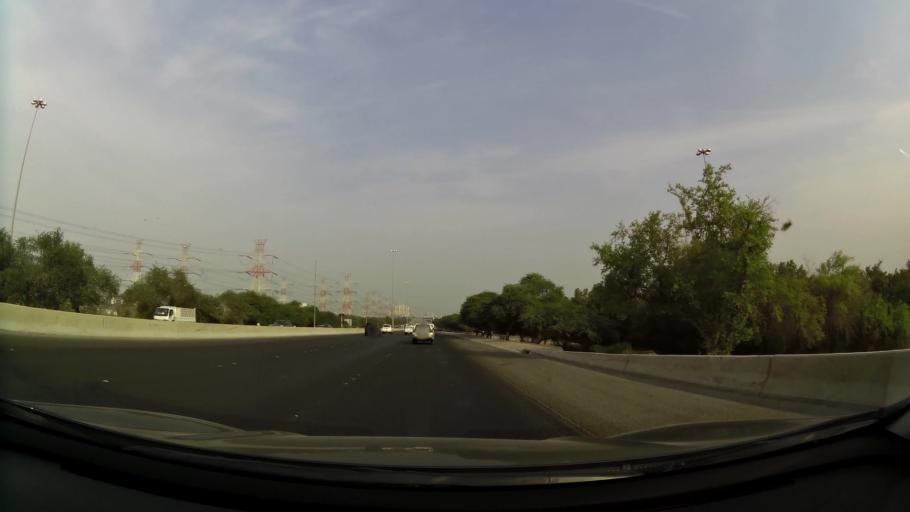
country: KW
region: Mubarak al Kabir
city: Sabah as Salim
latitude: 29.2645
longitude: 48.0453
